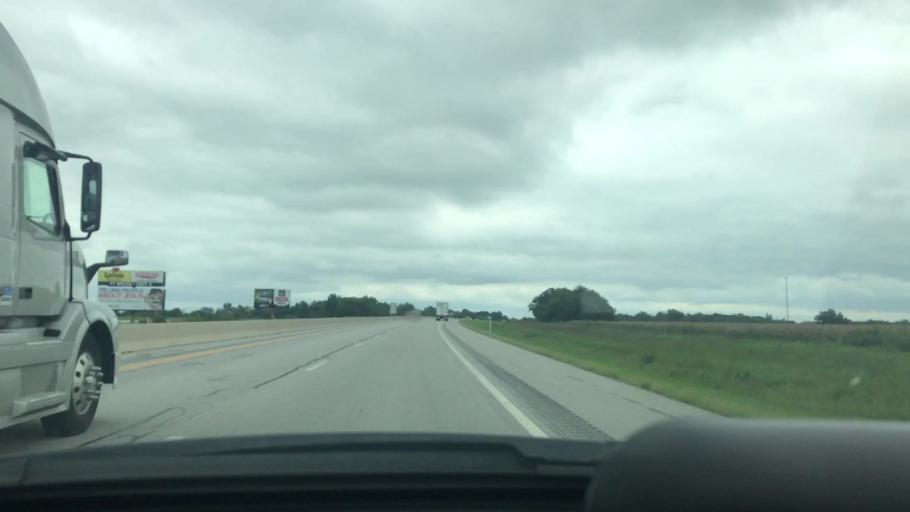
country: US
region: Oklahoma
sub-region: Ottawa County
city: Miami
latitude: 36.8885
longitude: -94.8358
